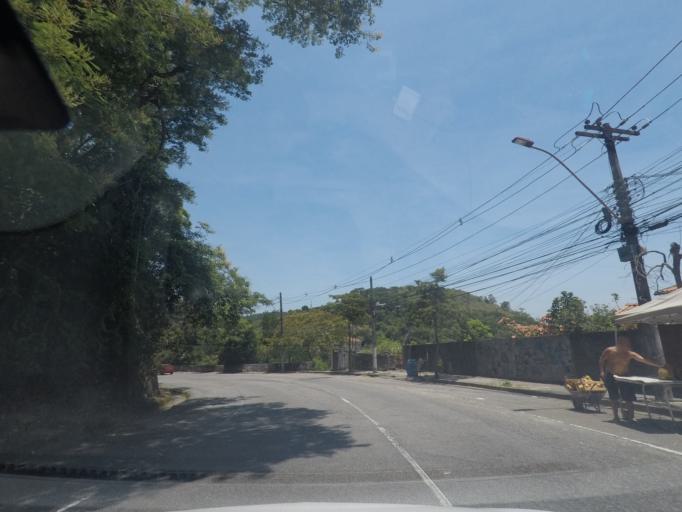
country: BR
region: Rio de Janeiro
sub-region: Niteroi
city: Niteroi
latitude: -22.9189
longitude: -43.0649
